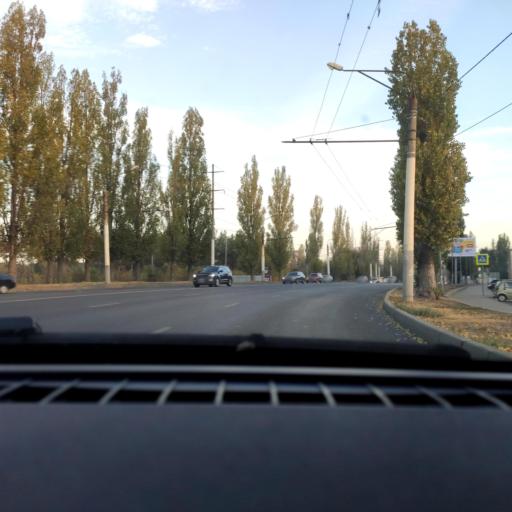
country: RU
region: Voronezj
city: Maslovka
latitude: 51.6024
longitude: 39.2373
